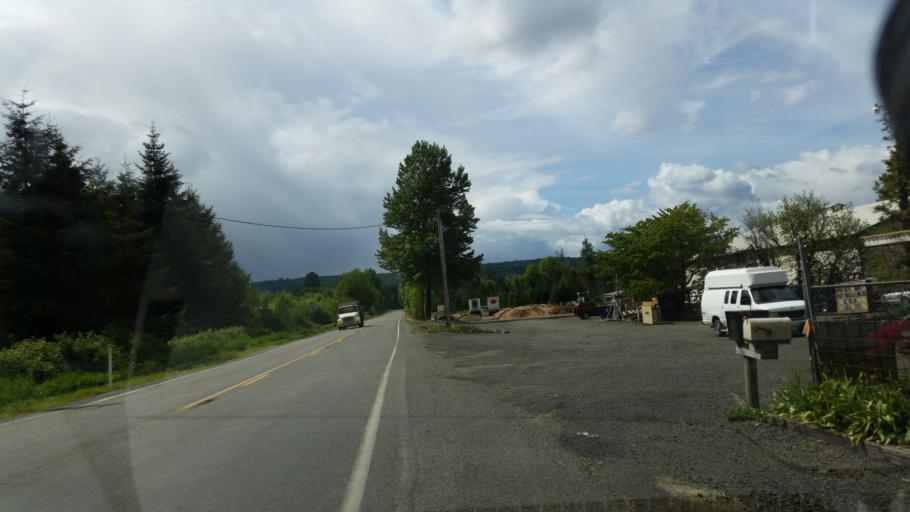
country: US
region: Washington
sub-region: Mason County
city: Shelton
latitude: 47.3187
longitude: -123.1338
